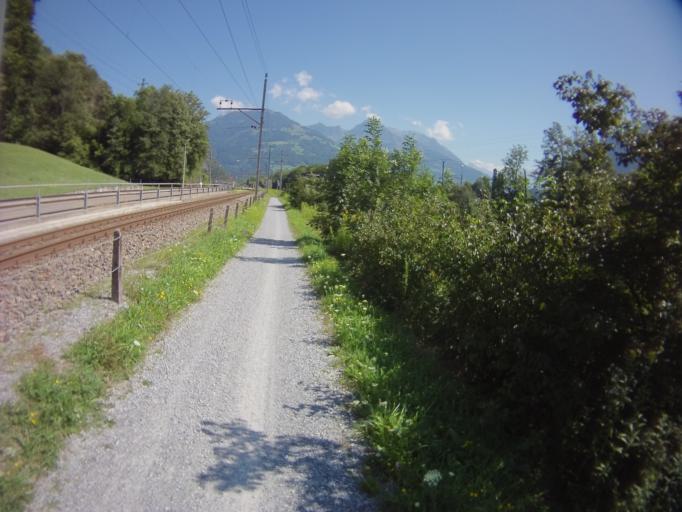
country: CH
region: Glarus
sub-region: Glarus
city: Niederurnen
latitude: 47.1407
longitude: 9.0524
